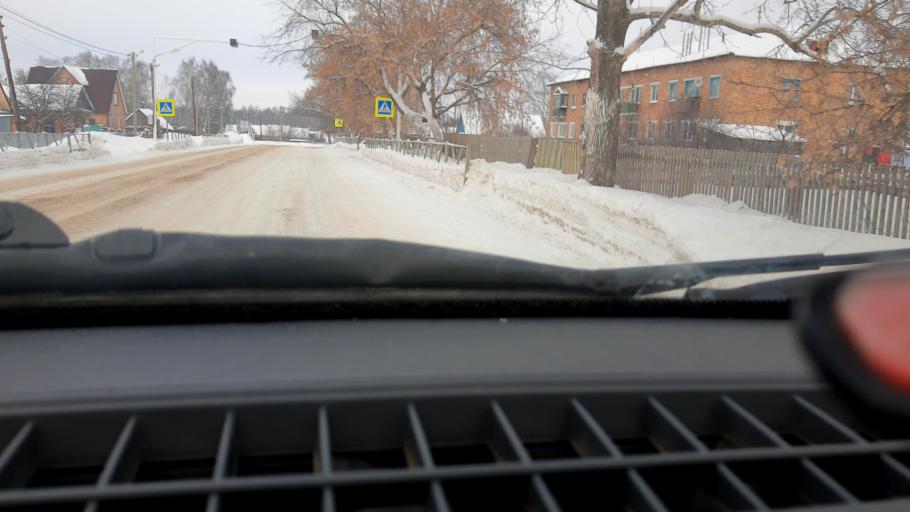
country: RU
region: Bashkortostan
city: Davlekanovo
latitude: 54.5778
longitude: 54.9375
